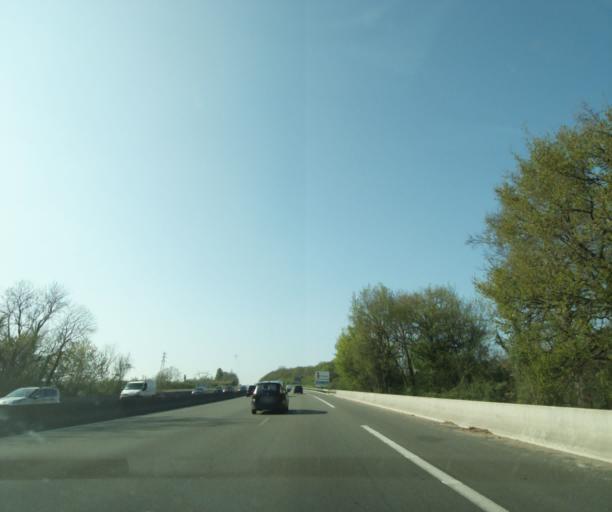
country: FR
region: Ile-de-France
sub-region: Departement de l'Essonne
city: Ormoy
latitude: 48.5783
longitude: 2.4633
